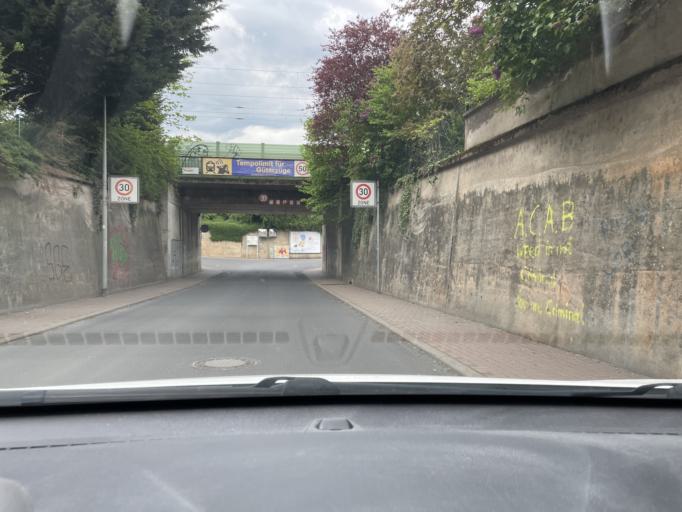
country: DE
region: Rheinland-Pfalz
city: Oestrich-Winkel
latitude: 50.0019
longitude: 8.0149
